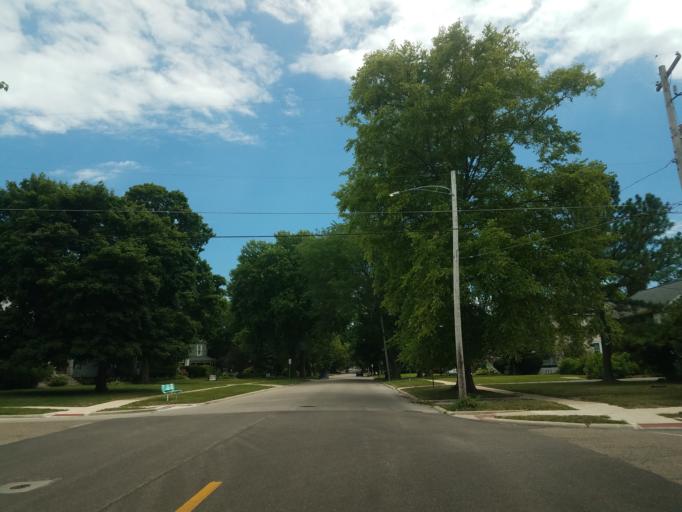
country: US
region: Illinois
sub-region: McLean County
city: Bloomington
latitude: 40.4782
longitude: -88.9721
